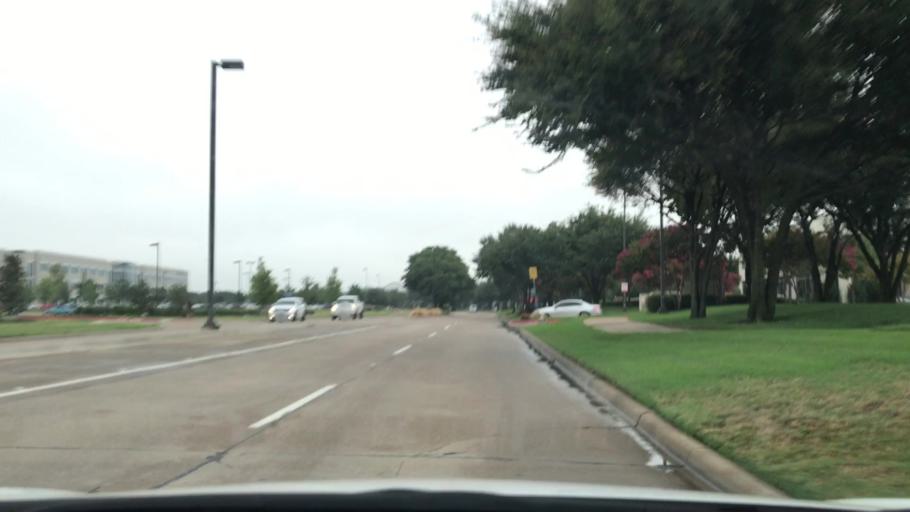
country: US
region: Texas
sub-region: Dallas County
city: Coppell
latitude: 32.9345
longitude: -97.0116
